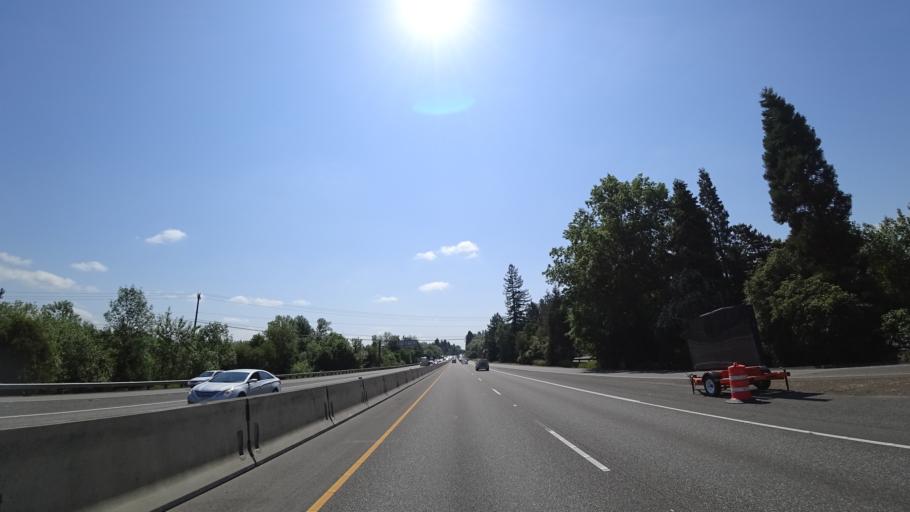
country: US
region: Oregon
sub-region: Washington County
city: Tigard
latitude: 45.4427
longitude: -122.7756
